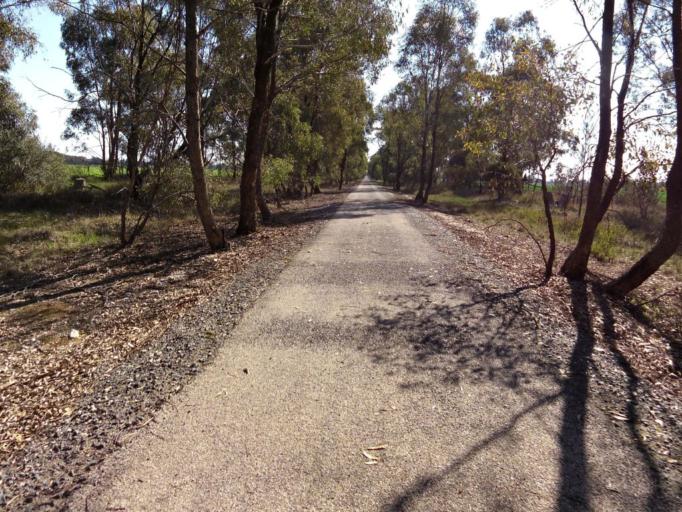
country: AU
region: New South Wales
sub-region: Corowa Shire
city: Corowa
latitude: -36.0255
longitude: 146.4314
